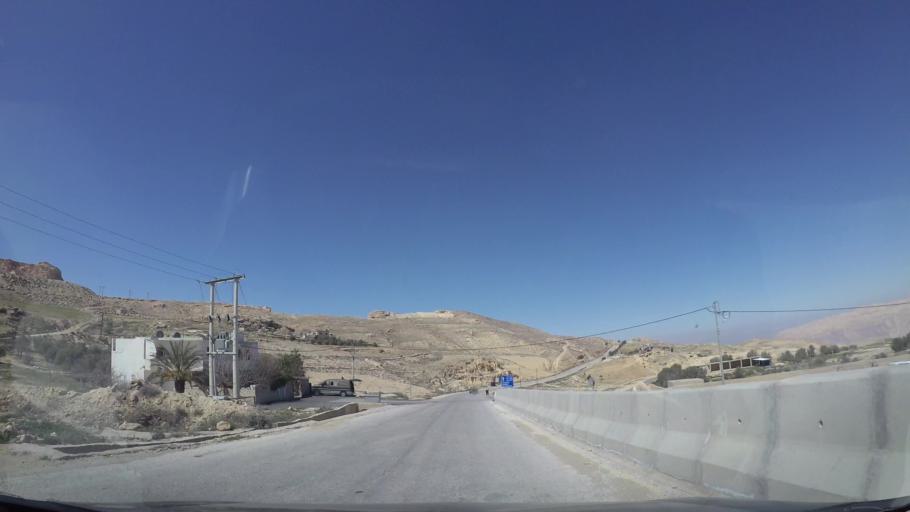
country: JO
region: Tafielah
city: At Tafilah
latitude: 30.8410
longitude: 35.5639
